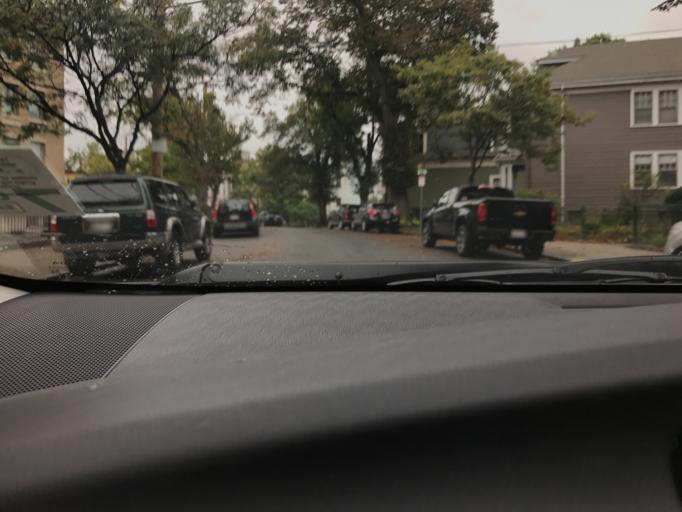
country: US
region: Massachusetts
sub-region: Suffolk County
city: South Boston
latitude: 42.3322
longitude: -71.0452
